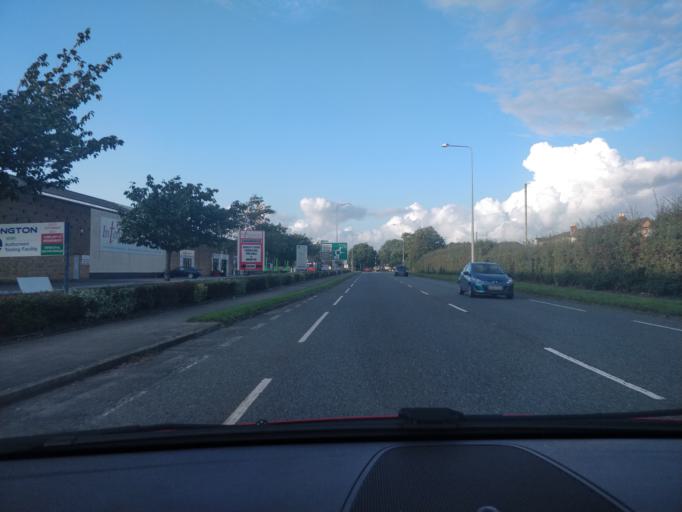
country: GB
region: England
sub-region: Lancashire
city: Tarleton
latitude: 53.7054
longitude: -2.7981
